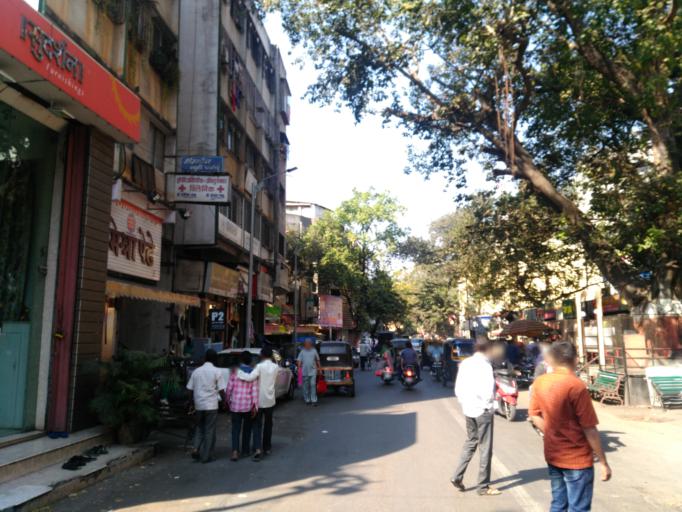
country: IN
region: Maharashtra
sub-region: Pune Division
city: Pune
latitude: 18.5149
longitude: 73.8501
